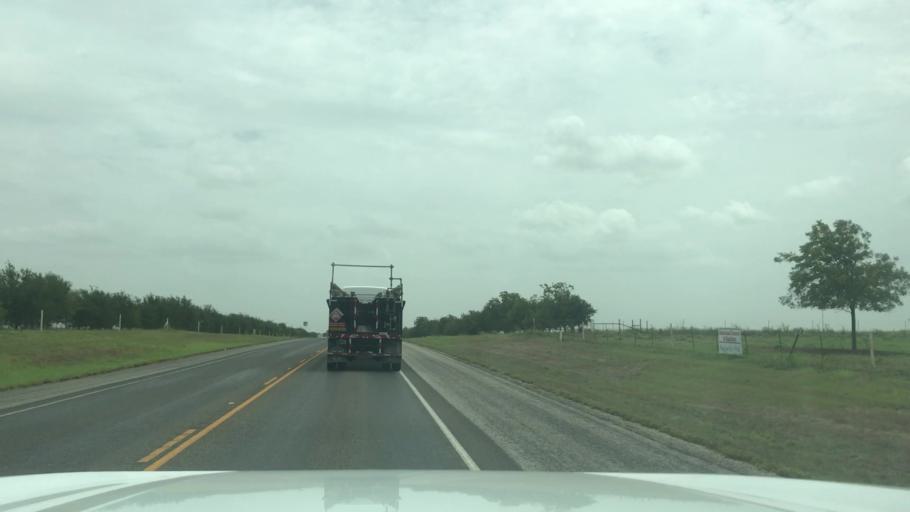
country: US
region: Texas
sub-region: Bosque County
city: Clifton
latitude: 31.8028
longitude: -97.6021
